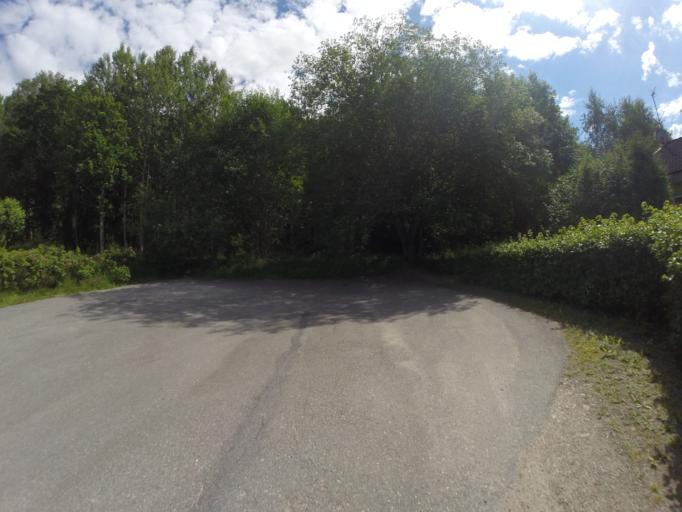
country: SE
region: Soedermanland
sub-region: Eskilstuna Kommun
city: Kvicksund
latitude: 59.4437
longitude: 16.3174
